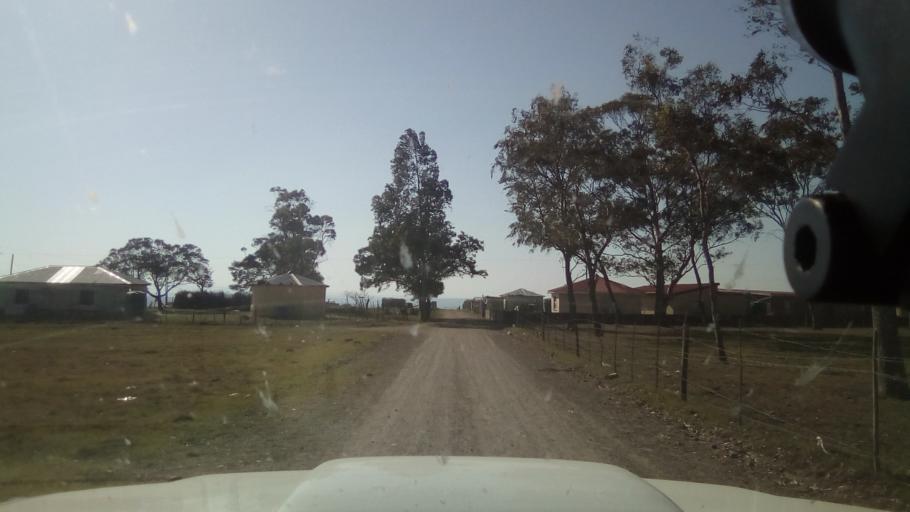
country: ZA
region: Eastern Cape
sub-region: Buffalo City Metropolitan Municipality
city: Bhisho
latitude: -32.9411
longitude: 27.3384
